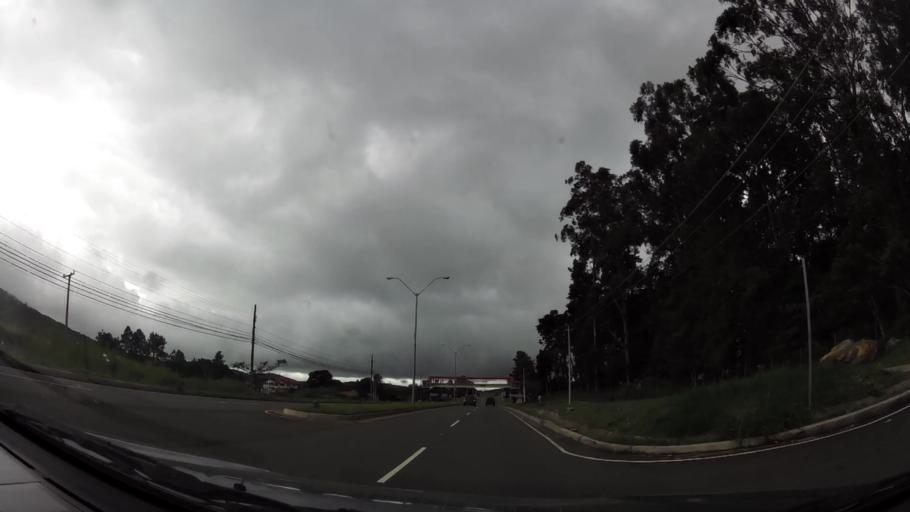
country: PA
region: Chiriqui
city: Palmira
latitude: 8.7466
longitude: -82.4325
